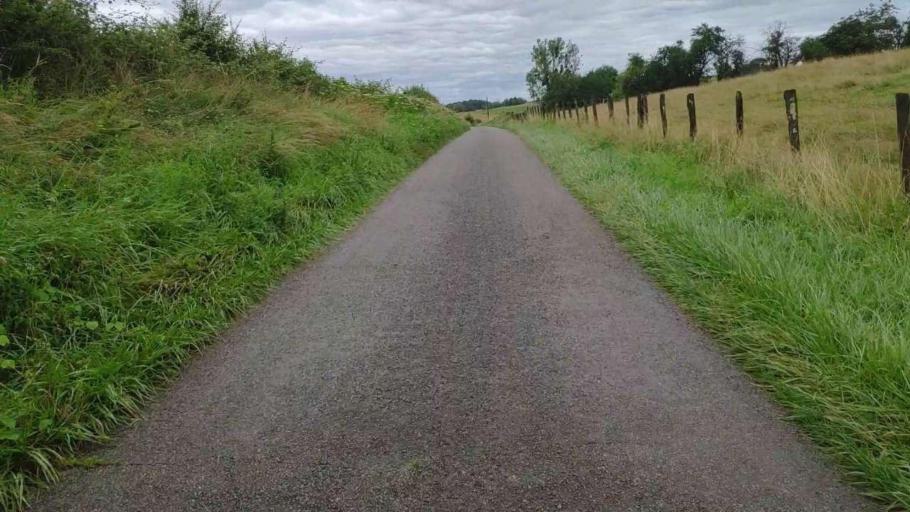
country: FR
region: Franche-Comte
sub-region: Departement du Jura
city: Perrigny
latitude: 46.7772
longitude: 5.5898
